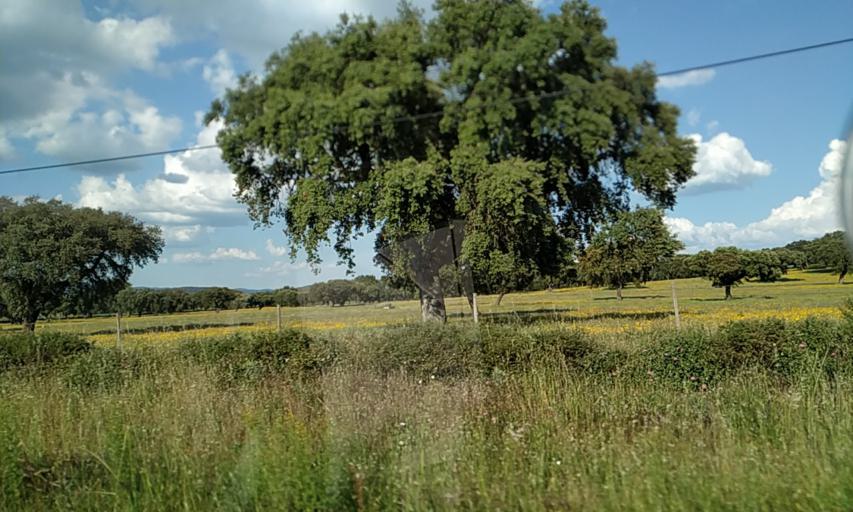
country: PT
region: Portalegre
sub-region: Portalegre
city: Urra
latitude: 39.1796
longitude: -7.4547
